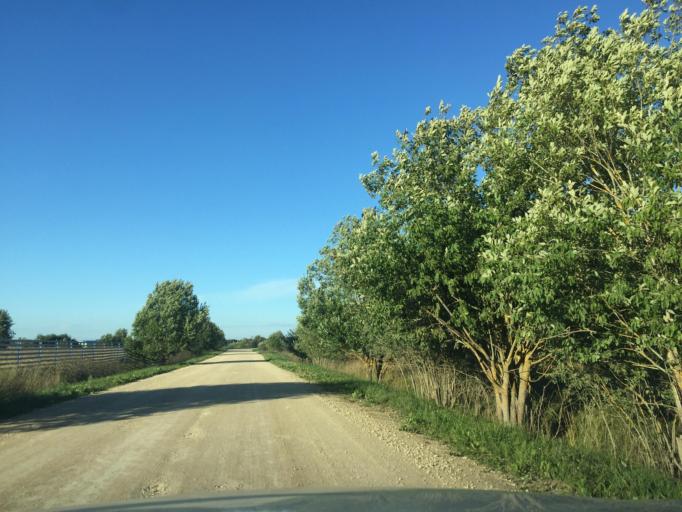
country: RU
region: Leningrad
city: Rozhdestveno
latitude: 59.3313
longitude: 29.9971
